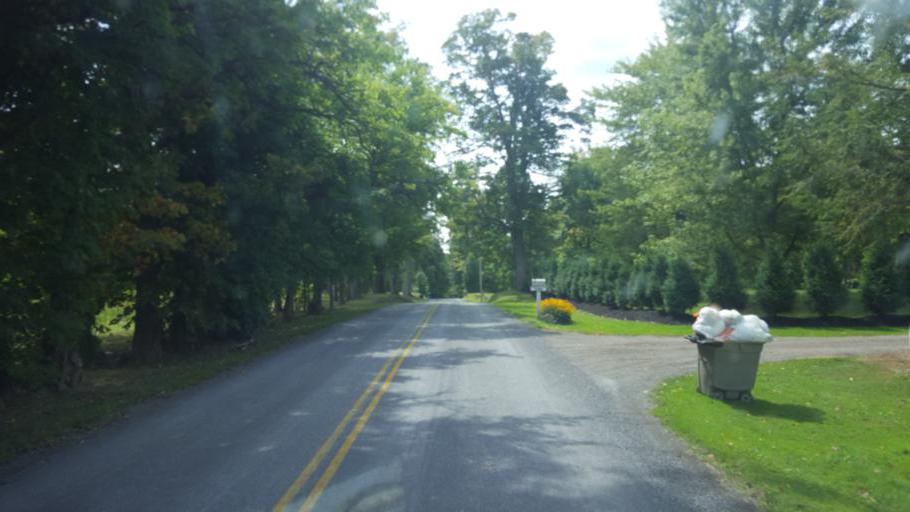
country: US
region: Ohio
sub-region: Geauga County
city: Middlefield
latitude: 41.4337
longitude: -80.9730
